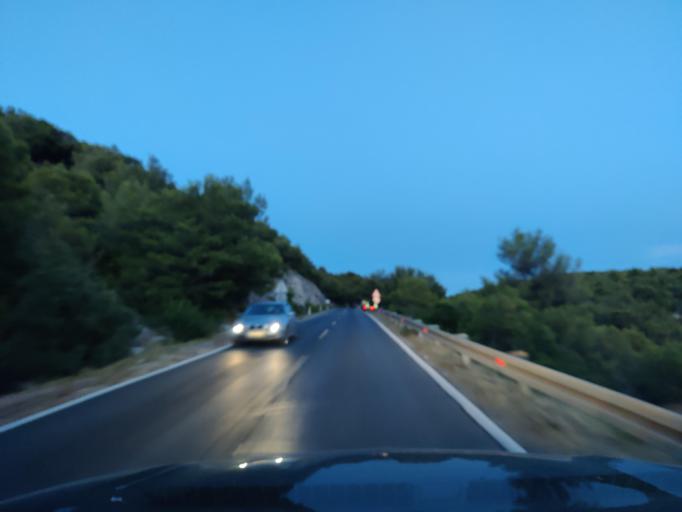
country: HR
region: Sibensko-Kniniska
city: Murter
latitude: 43.7982
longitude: 15.6146
